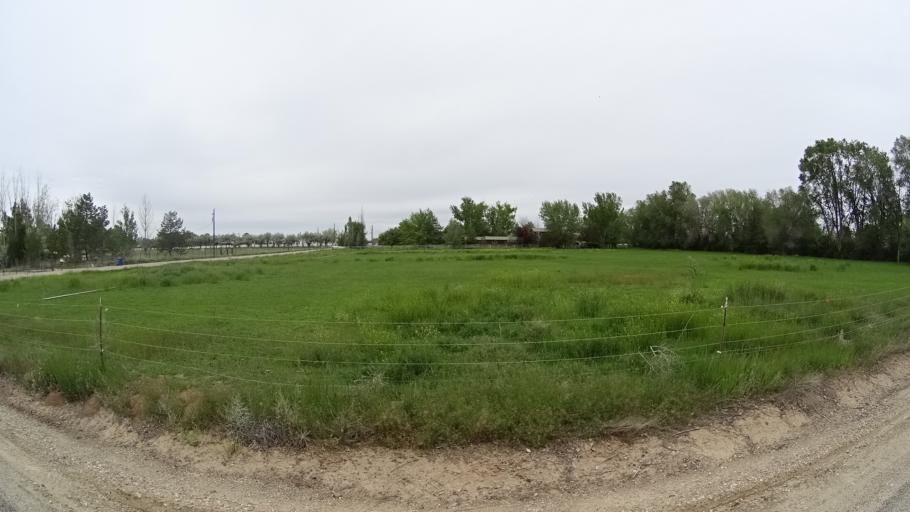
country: US
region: Idaho
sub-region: Ada County
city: Kuna
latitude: 43.4936
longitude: -116.3388
